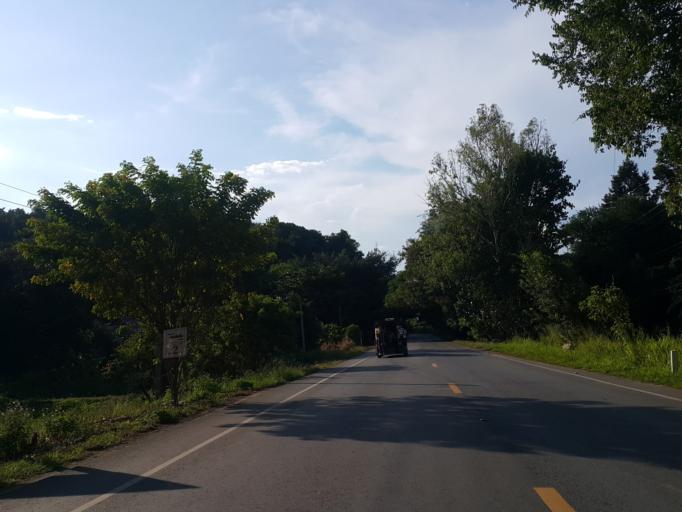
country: TH
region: Chiang Mai
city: Mae Taeng
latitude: 19.1148
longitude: 99.0119
